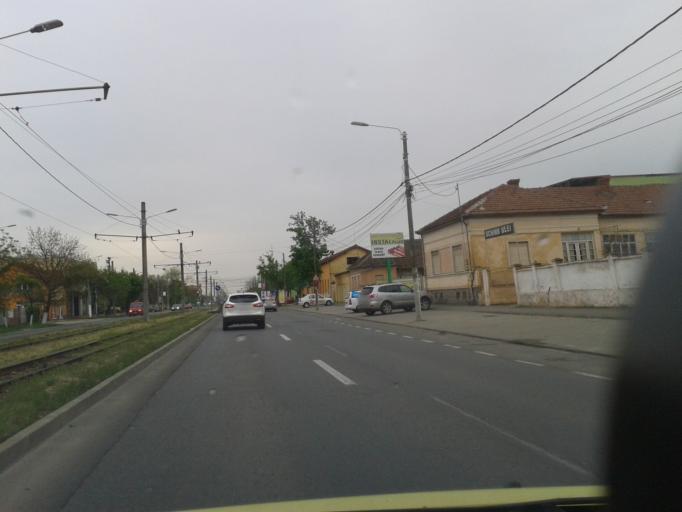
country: RO
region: Arad
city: Arad
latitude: 46.1771
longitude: 21.3578
